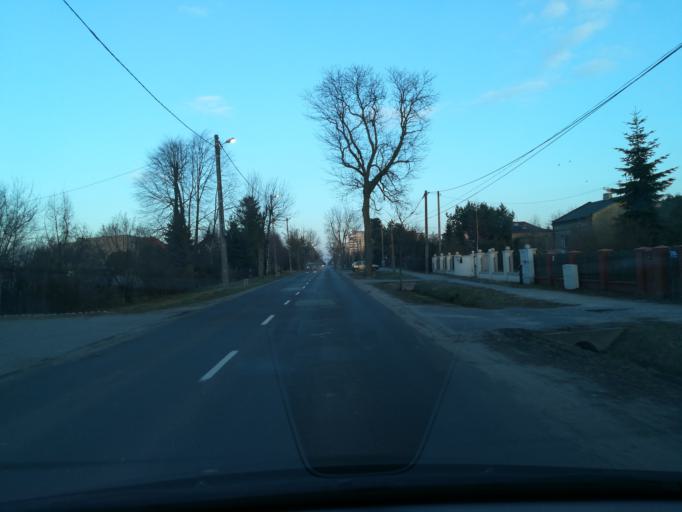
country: PL
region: Lodz Voivodeship
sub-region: Piotrkow Trybunalski
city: Piotrkow Trybunalski
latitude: 51.4110
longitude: 19.6500
